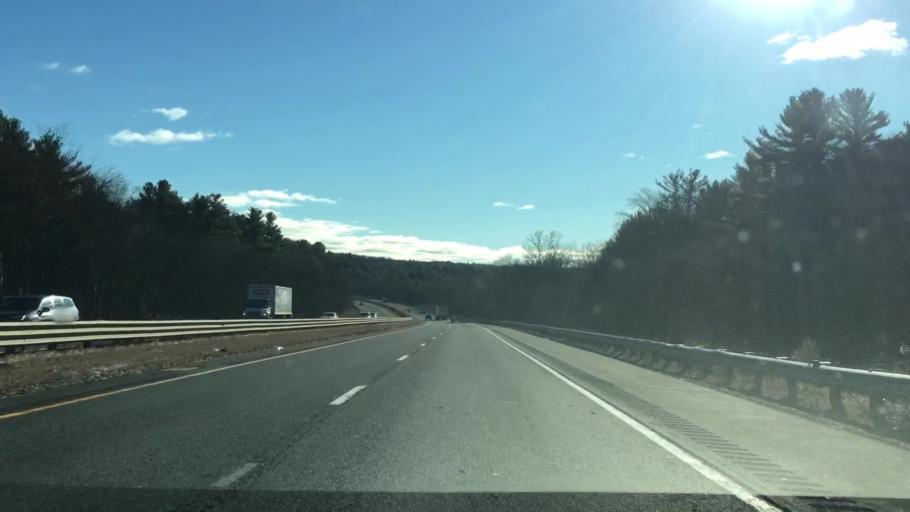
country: US
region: Massachusetts
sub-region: Worcester County
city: Fiskdale
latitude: 42.1395
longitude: -72.1339
